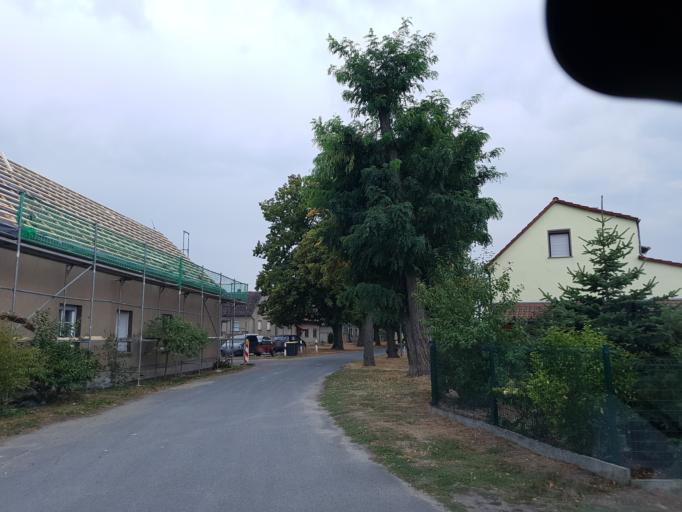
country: DE
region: Brandenburg
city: Herzberg
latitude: 51.6989
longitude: 13.2649
